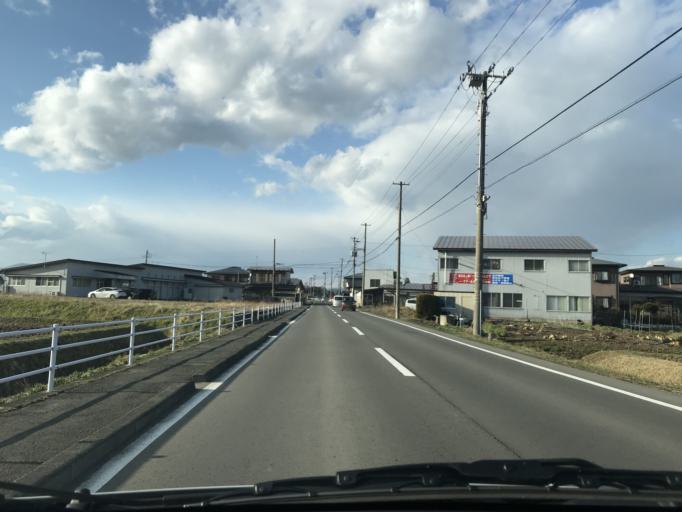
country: JP
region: Iwate
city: Kitakami
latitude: 39.3089
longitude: 141.0707
